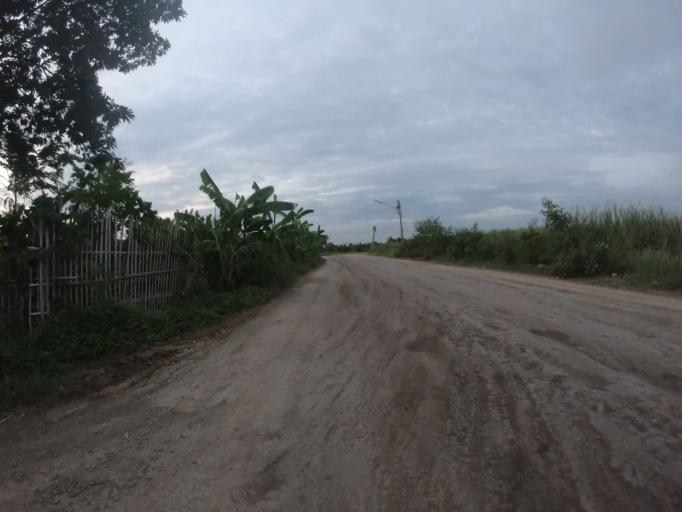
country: TH
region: Pathum Thani
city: Ban Lam Luk Ka
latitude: 14.0106
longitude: 100.8007
